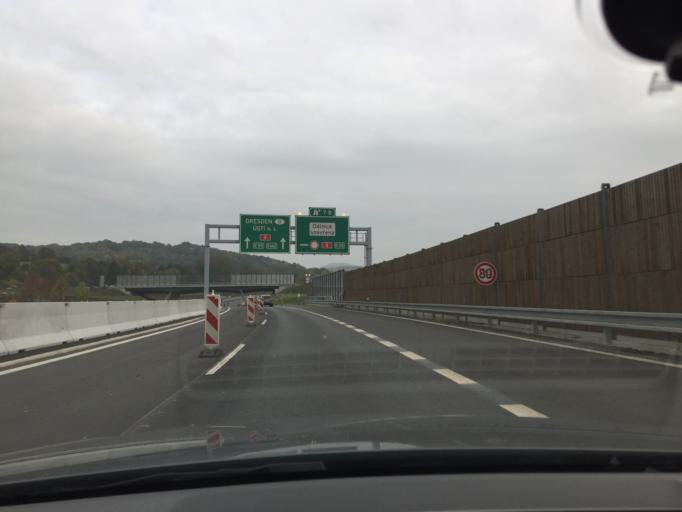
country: CZ
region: Ustecky
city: Rehlovice
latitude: 50.6136
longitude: 13.9601
